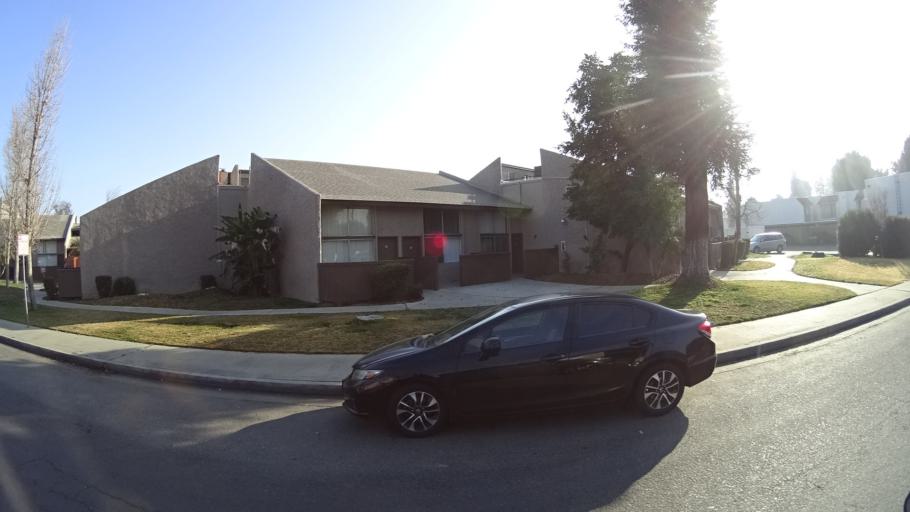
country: US
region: California
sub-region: Kern County
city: Bakersfield
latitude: 35.3510
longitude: -119.0590
